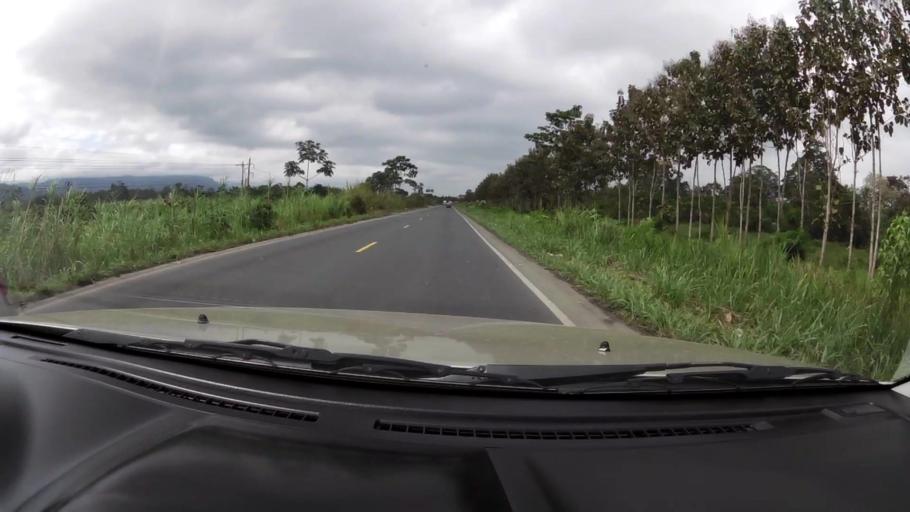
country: EC
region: Guayas
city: Naranjal
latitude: -2.7064
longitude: -79.6560
